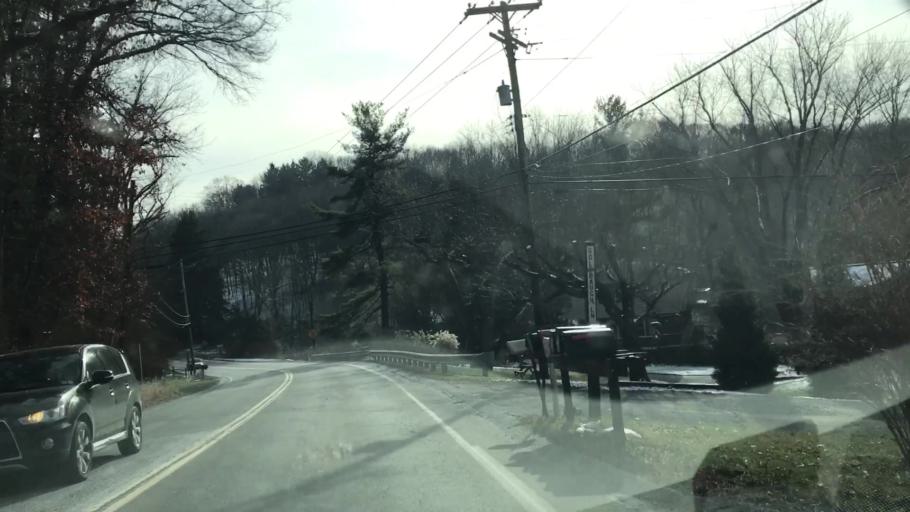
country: US
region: Pennsylvania
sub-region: Allegheny County
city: Franklin Park
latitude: 40.5936
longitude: -80.0768
